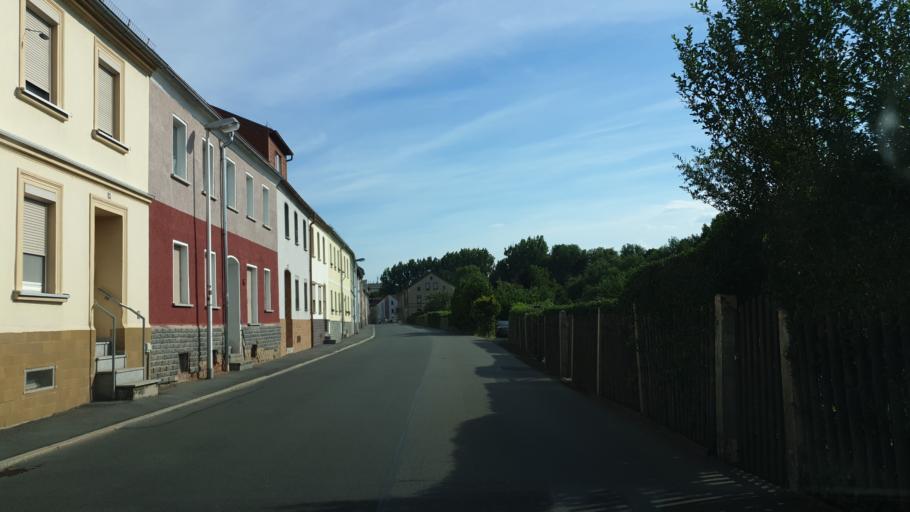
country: DE
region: Thuringia
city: Gera
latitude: 50.8385
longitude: 12.0787
